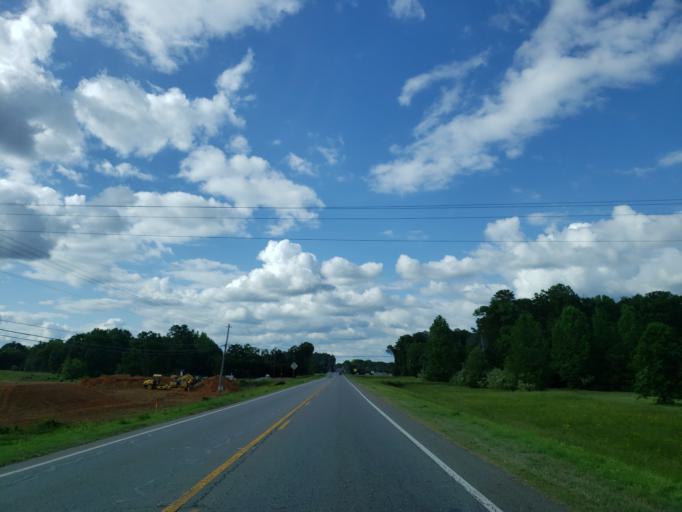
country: US
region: Georgia
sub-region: Bartow County
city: Cartersville
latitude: 34.2366
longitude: -84.8566
